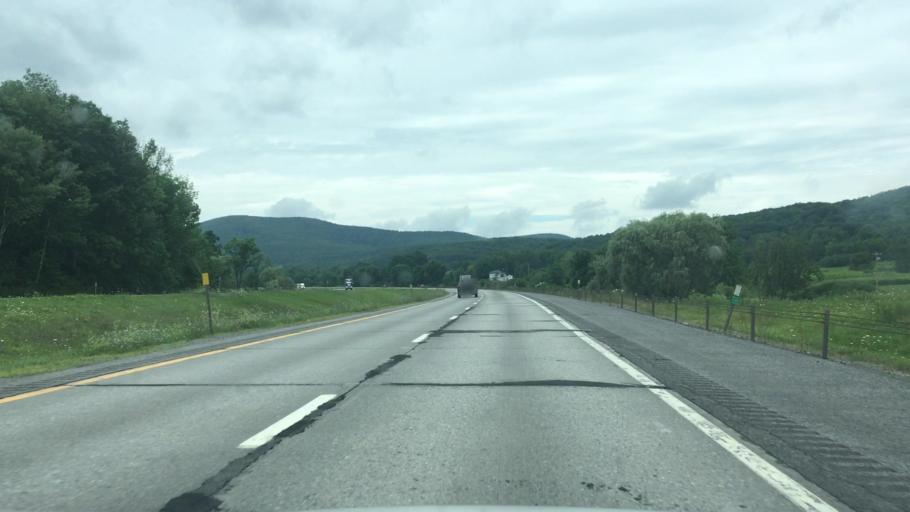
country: US
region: New York
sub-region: Schoharie County
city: Cobleskill
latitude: 42.6474
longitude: -74.5959
